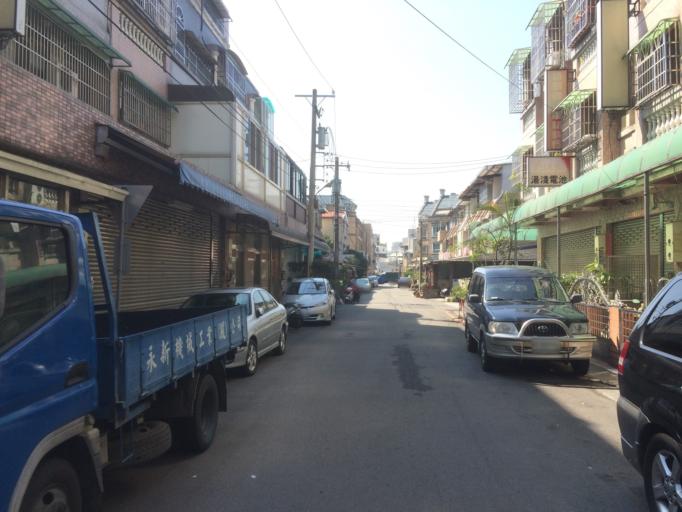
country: TW
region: Taiwan
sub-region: Taichung City
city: Taichung
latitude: 24.1850
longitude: 120.7021
